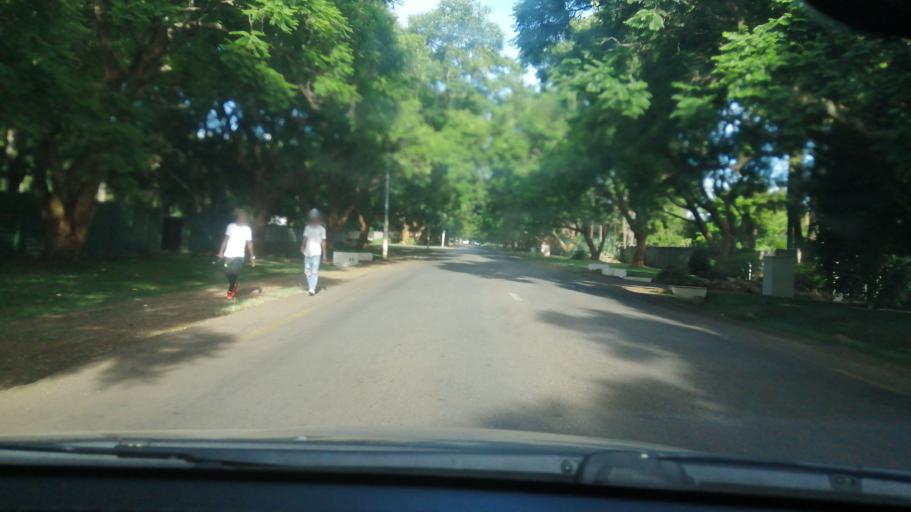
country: ZW
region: Harare
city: Harare
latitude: -17.7631
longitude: 31.0715
